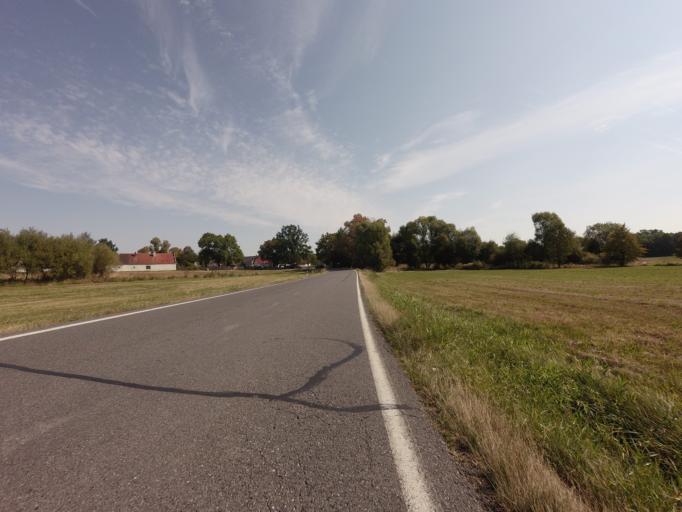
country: CZ
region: Jihocesky
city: Bernartice
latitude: 49.3558
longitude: 14.3767
